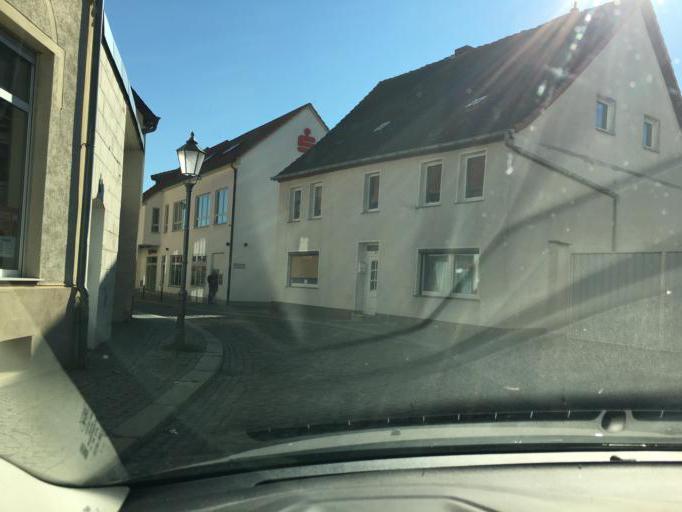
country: DE
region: Saxony-Anhalt
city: Wanzleben
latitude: 52.0621
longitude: 11.4399
